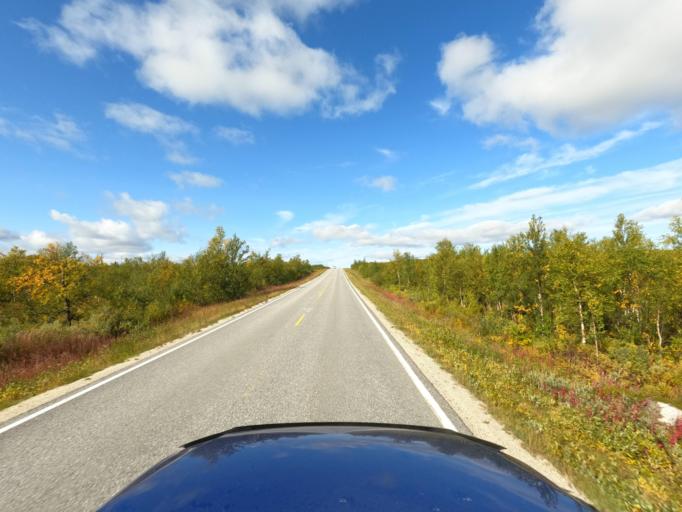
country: NO
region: Finnmark Fylke
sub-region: Karasjok
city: Karasjohka
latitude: 69.5522
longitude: 25.4090
